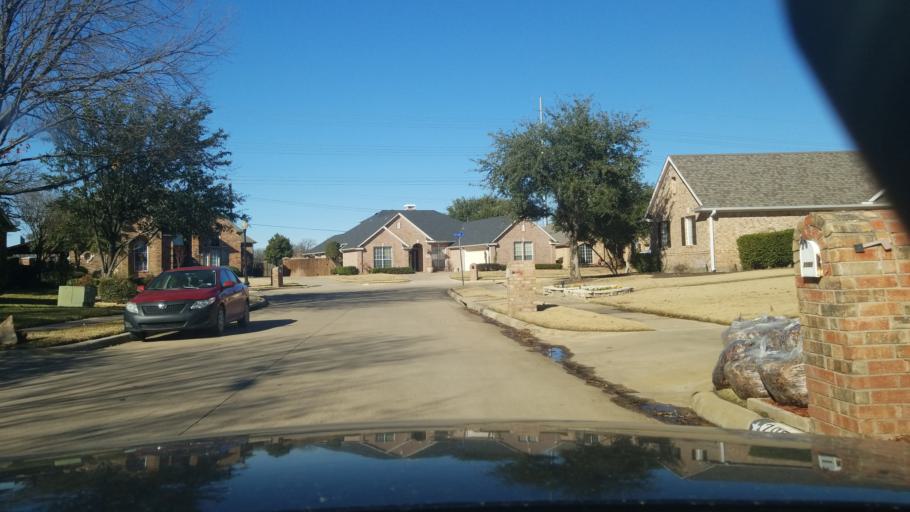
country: US
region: Texas
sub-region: Denton County
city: Corinth
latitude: 33.1618
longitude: -97.0819
